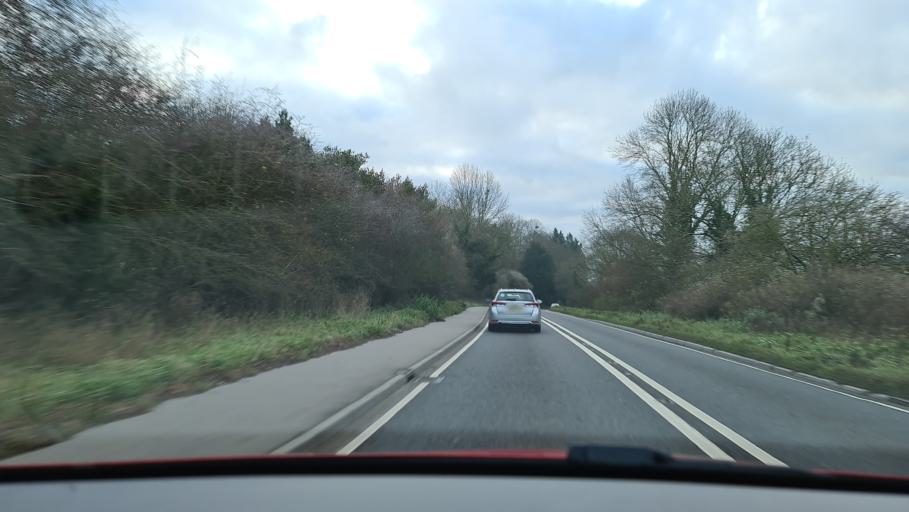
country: GB
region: England
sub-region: Buckinghamshire
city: Princes Risborough
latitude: 51.6636
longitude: -0.8088
